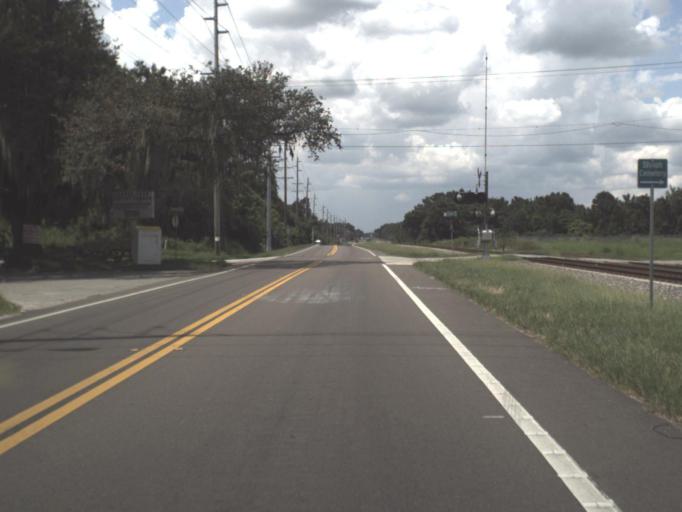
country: US
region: Florida
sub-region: Hillsborough County
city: Plant City
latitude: 28.0397
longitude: -82.1270
